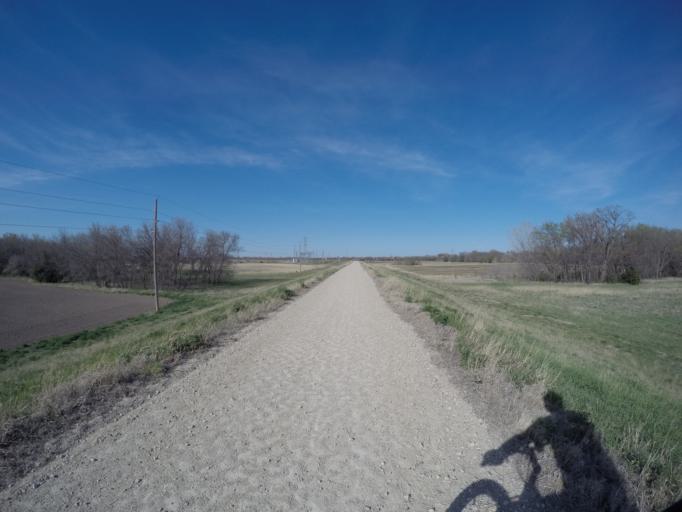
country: US
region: Kansas
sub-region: Saline County
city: Salina
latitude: 38.8463
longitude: -97.5767
